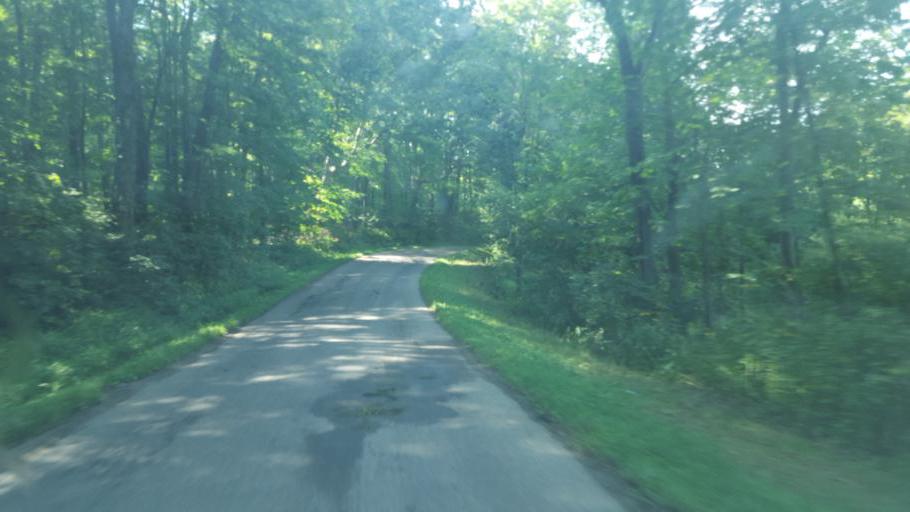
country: US
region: Ohio
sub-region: Knox County
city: Danville
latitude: 40.4745
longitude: -82.3016
